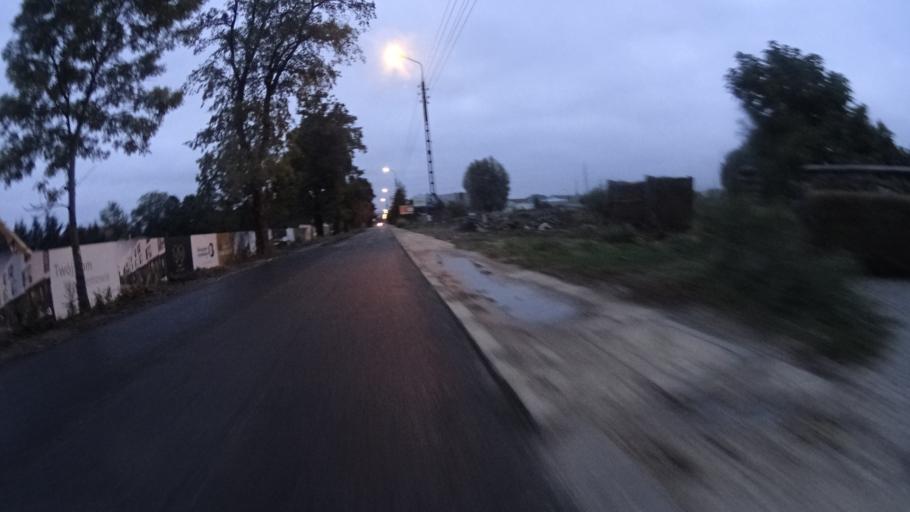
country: PL
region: Masovian Voivodeship
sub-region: Warszawa
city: Ursus
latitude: 52.2224
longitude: 20.8948
